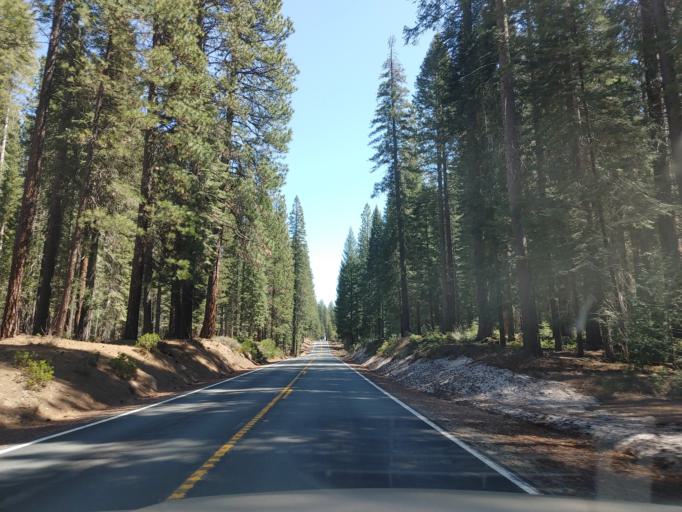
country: US
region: California
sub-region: Siskiyou County
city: McCloud
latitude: 41.2670
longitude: -121.9198
